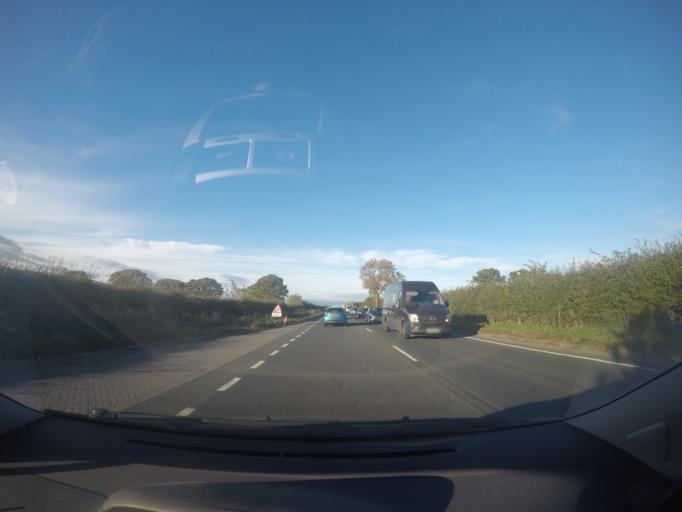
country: GB
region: England
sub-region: City of York
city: Nether Poppleton
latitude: 53.9601
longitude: -1.1505
